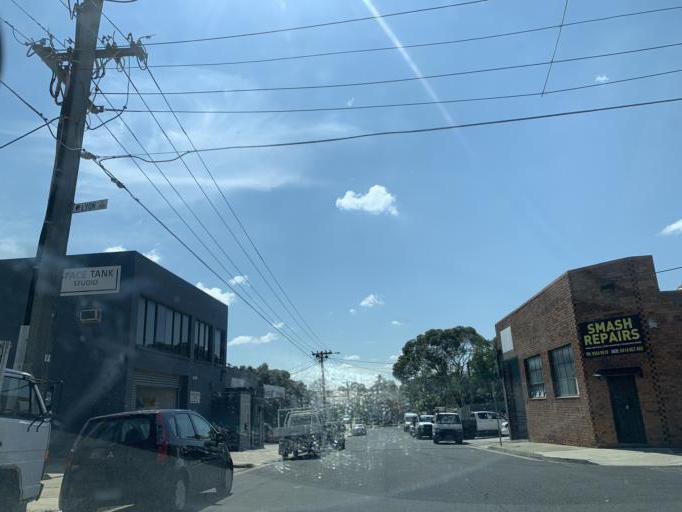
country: AU
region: Victoria
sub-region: Moreland
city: Coburg North
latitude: -37.7257
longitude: 144.9549
